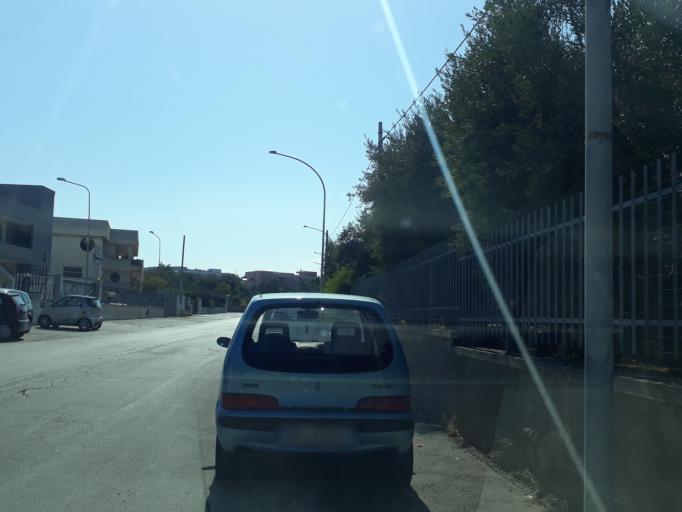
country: IT
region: Apulia
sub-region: Provincia di Bari
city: Monopoli
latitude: 40.9413
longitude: 17.3033
